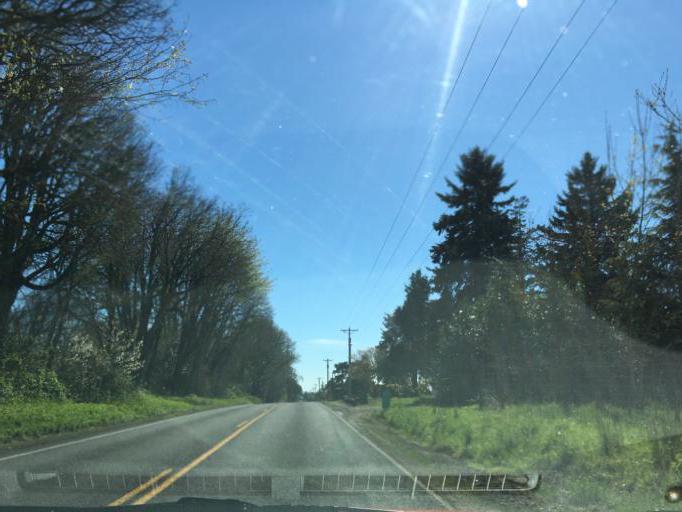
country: US
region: Oregon
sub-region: Marion County
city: Hubbard
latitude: 45.1689
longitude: -122.7226
